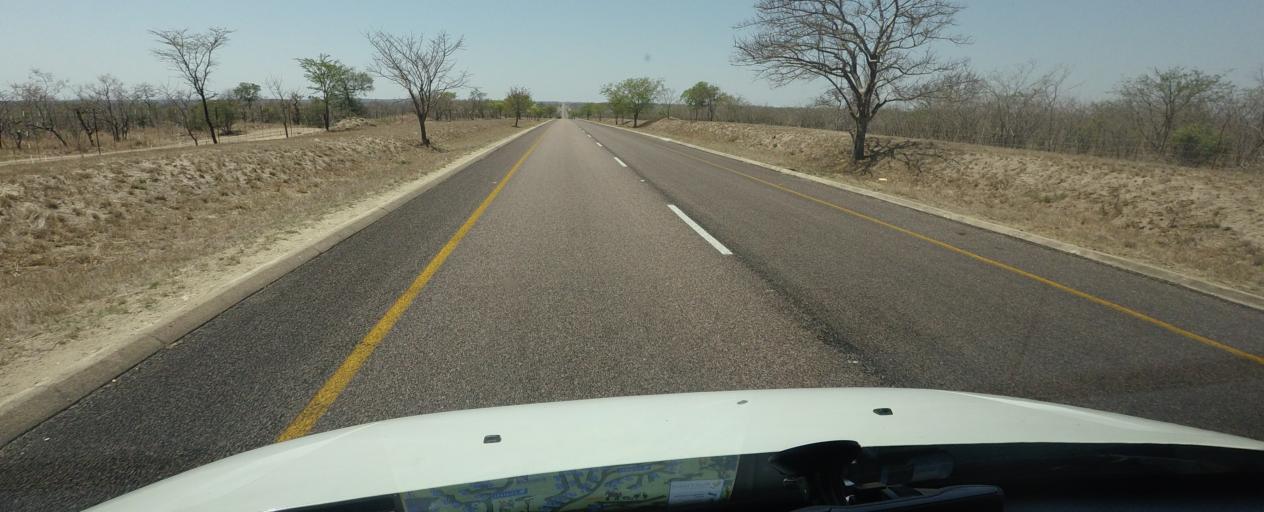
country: ZA
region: Limpopo
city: Thulamahashi
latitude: -24.5532
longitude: 31.2799
